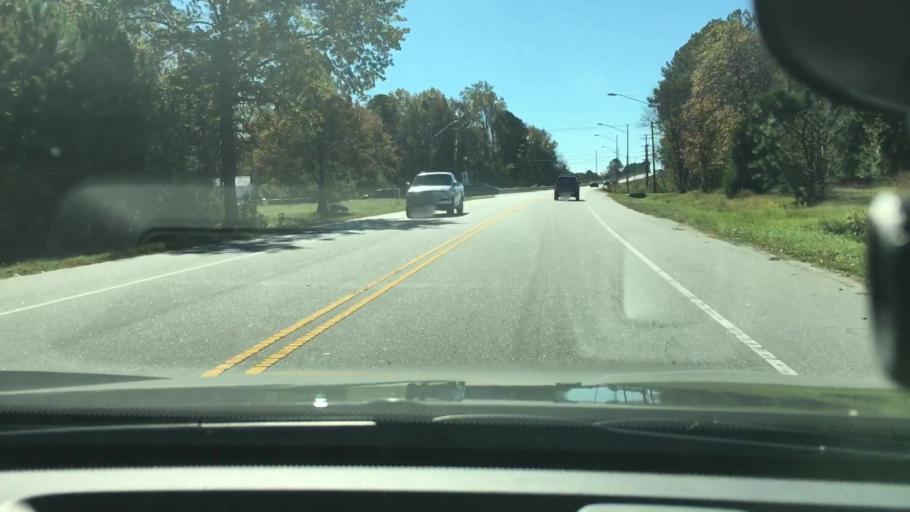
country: US
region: North Carolina
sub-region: Edgecombe County
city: Tarboro
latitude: 35.9150
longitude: -77.5623
